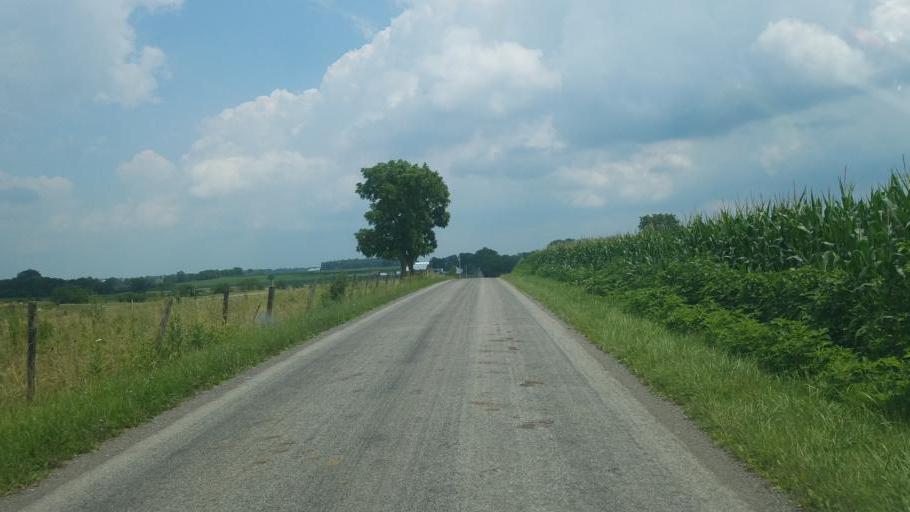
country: US
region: Ohio
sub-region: Hardin County
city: Kenton
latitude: 40.5930
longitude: -83.6272
